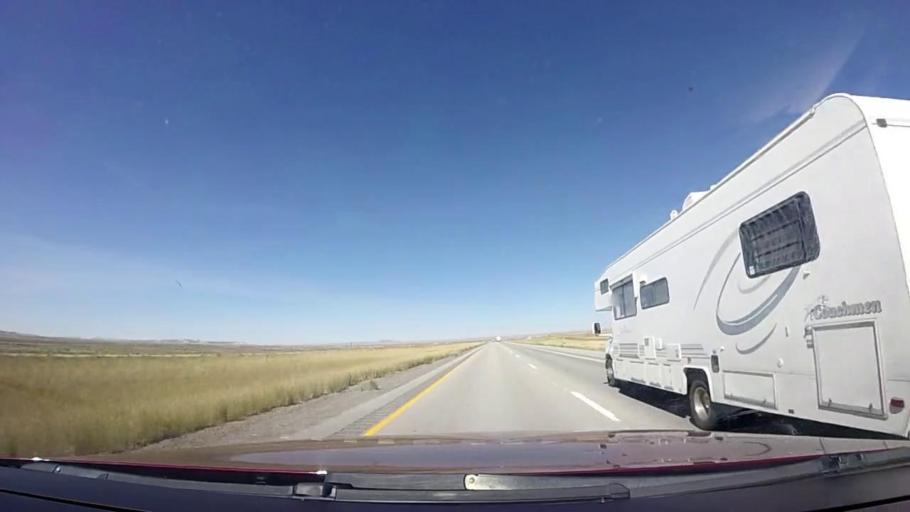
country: US
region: Wyoming
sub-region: Sweetwater County
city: Rock Springs
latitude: 41.6314
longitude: -108.3422
